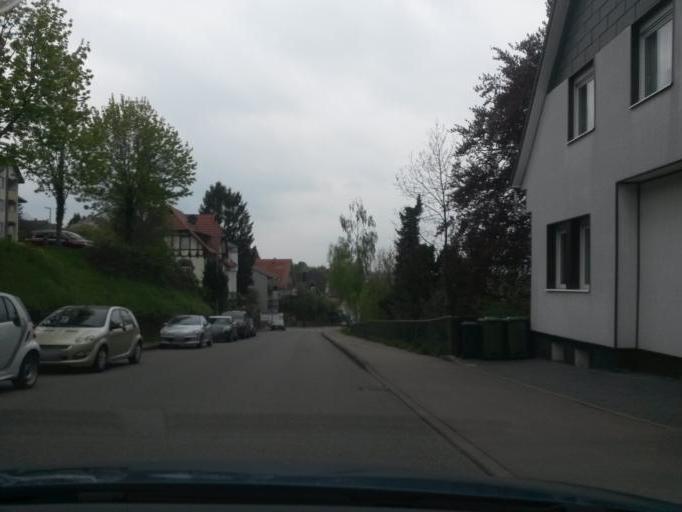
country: DE
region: Baden-Wuerttemberg
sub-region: Karlsruhe Region
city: Birkenfeld
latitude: 48.8709
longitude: 8.6432
